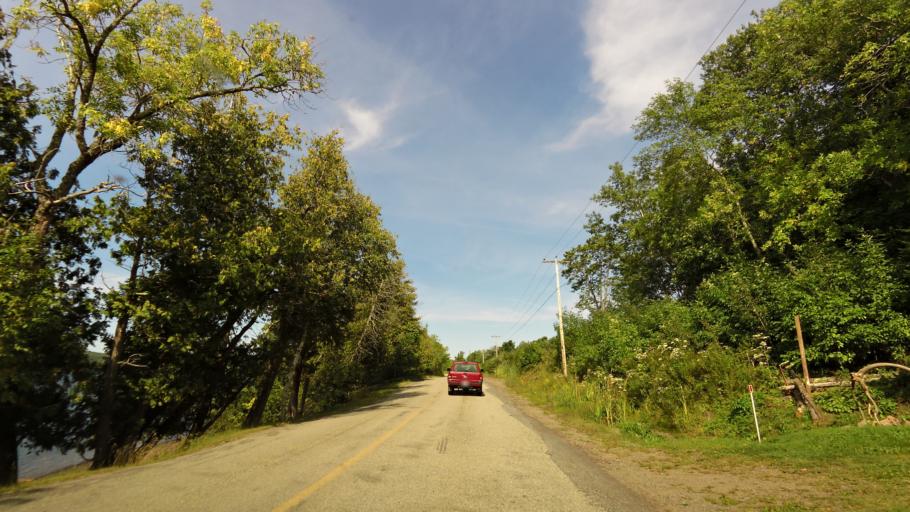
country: CA
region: New Brunswick
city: Hampton
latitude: 45.5975
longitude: -65.9132
